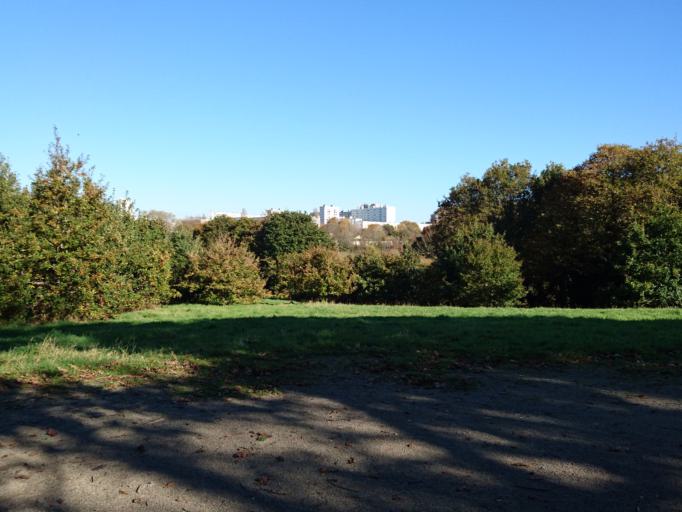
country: FR
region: Brittany
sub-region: Departement du Finistere
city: Bohars
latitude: 48.4009
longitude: -4.5225
